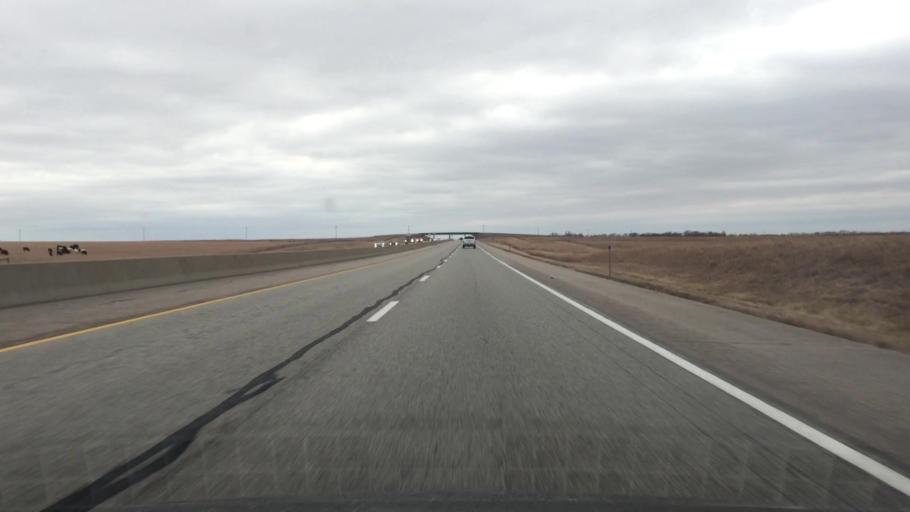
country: US
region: Kansas
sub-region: Butler County
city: El Dorado
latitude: 37.9904
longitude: -96.7018
